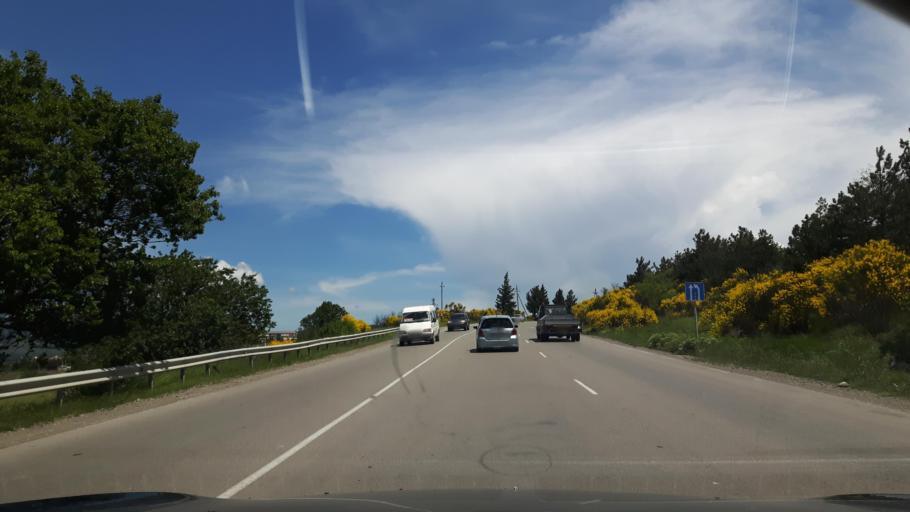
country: GE
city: Didi Lilo
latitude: 41.6952
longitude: 45.0393
